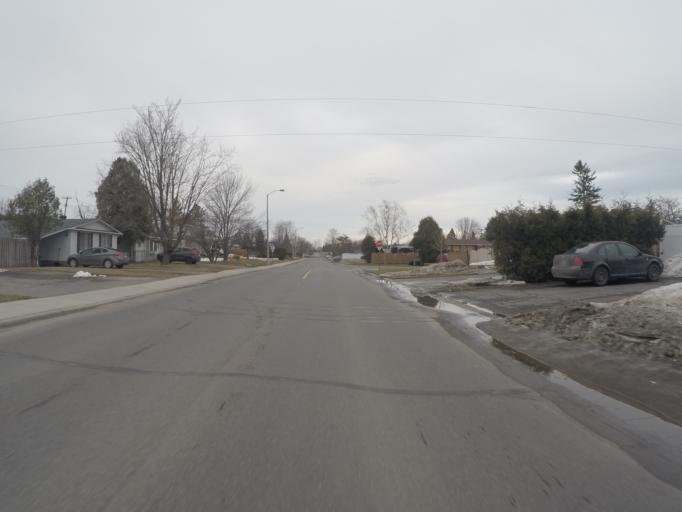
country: CA
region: Quebec
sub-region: Outaouais
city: Gatineau
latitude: 45.4725
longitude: -75.5051
